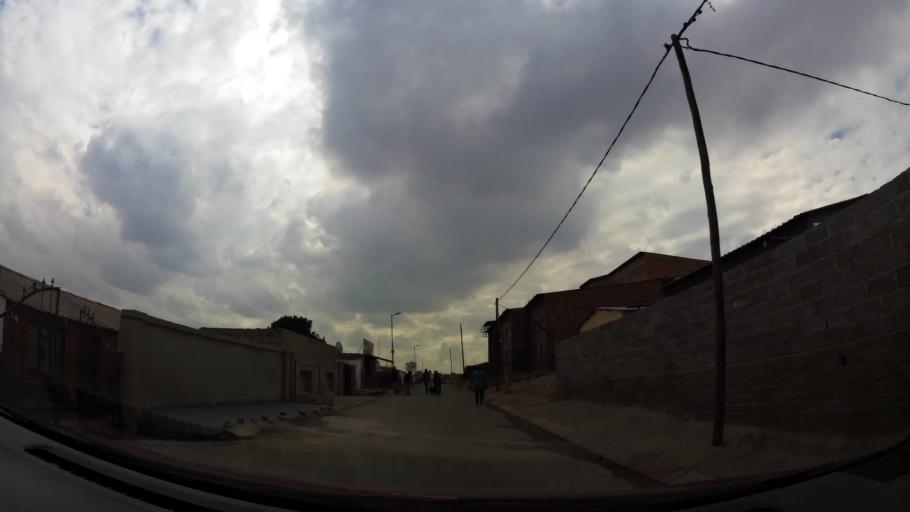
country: ZA
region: Gauteng
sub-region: City of Johannesburg Metropolitan Municipality
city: Soweto
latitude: -26.2544
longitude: 27.8235
